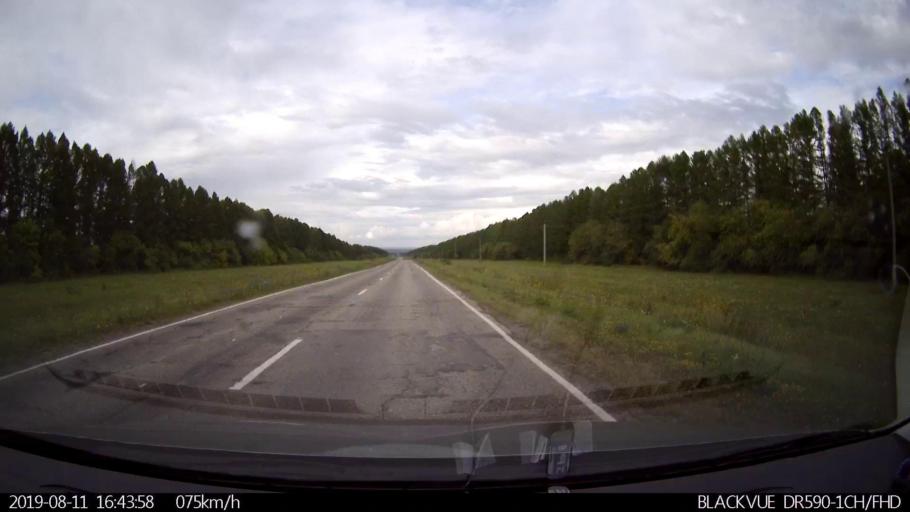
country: RU
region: Ulyanovsk
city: Mayna
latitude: 54.1745
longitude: 47.6771
